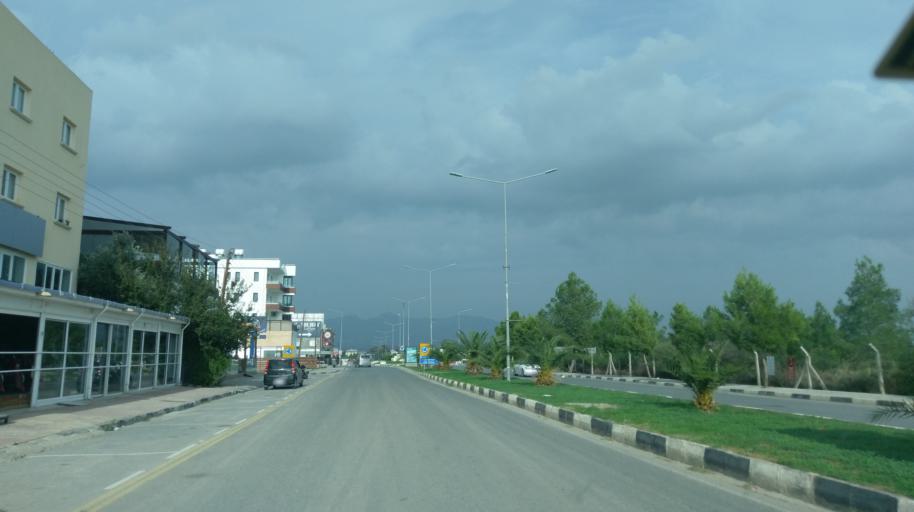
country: CY
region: Lefkosia
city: Nicosia
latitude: 35.1896
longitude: 33.3263
